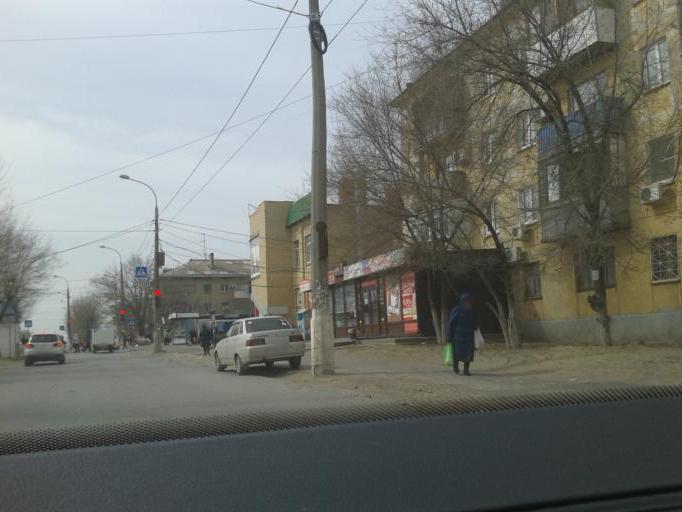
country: RU
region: Volgograd
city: Gorodishche
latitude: 48.7677
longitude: 44.4793
